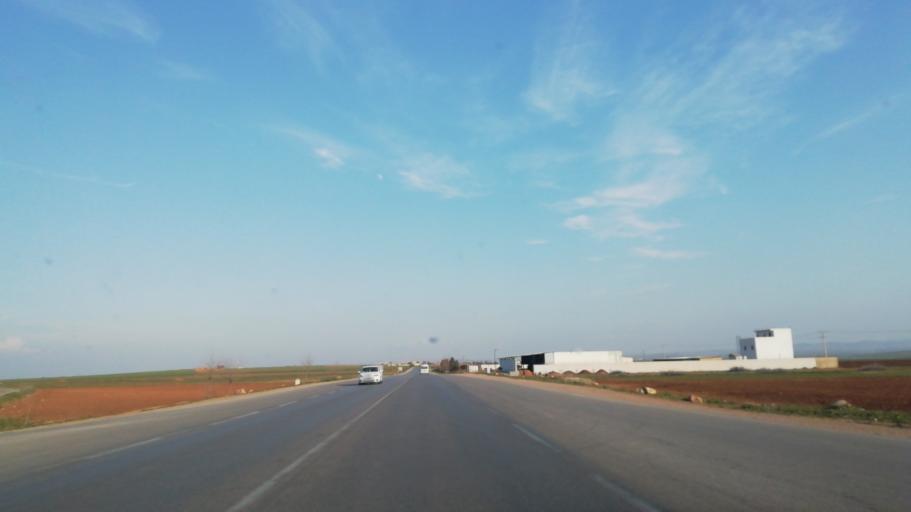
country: DZ
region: Relizane
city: Relizane
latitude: 35.8935
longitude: 0.6429
